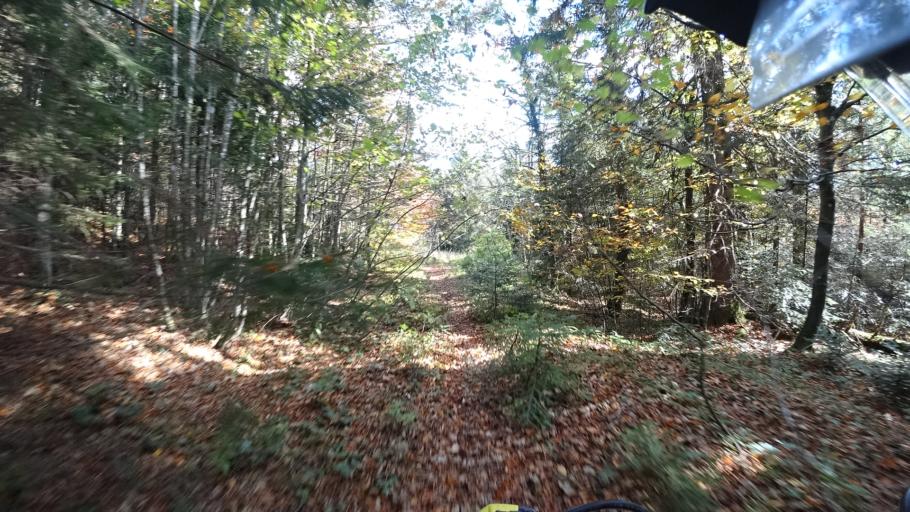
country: HR
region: Karlovacka
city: Plaski
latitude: 45.0685
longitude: 15.3120
